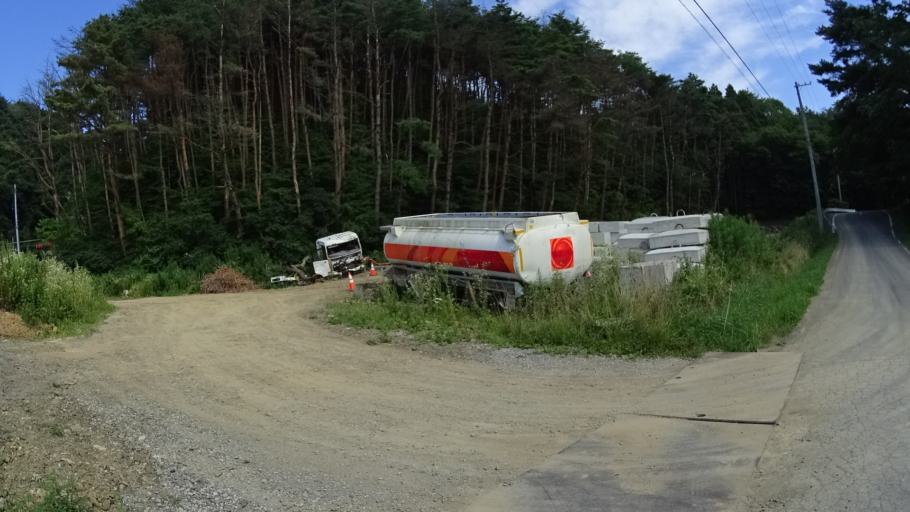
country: JP
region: Iwate
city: Ofunato
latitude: 38.8739
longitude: 141.6026
